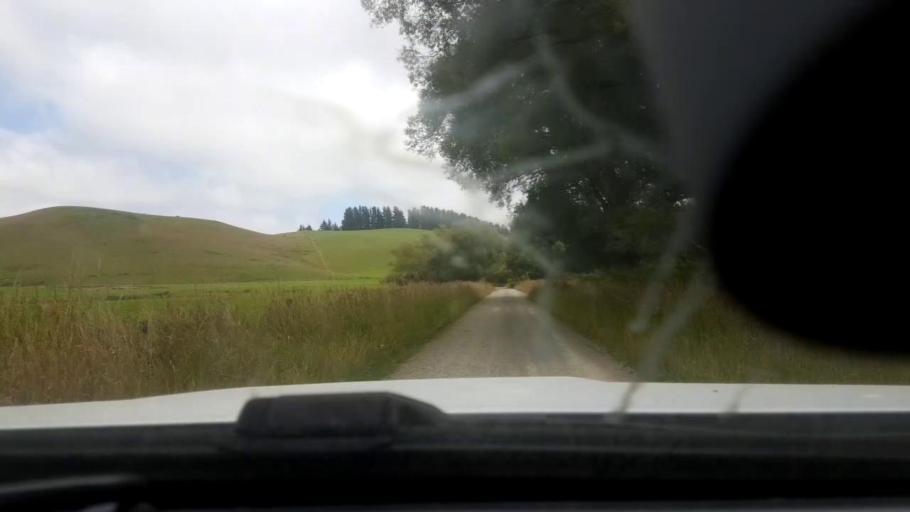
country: NZ
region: Canterbury
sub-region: Timaru District
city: Pleasant Point
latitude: -44.1549
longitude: 171.0955
